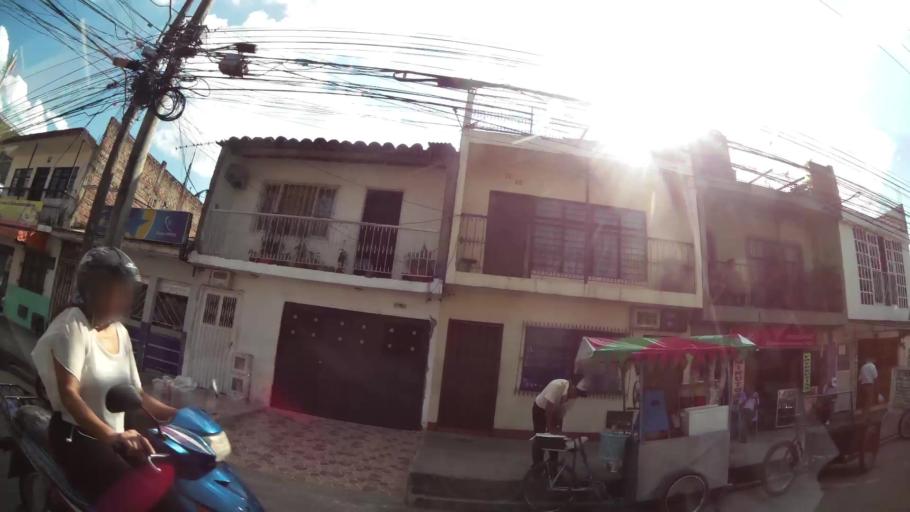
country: CO
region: Valle del Cauca
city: Cali
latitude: 3.4208
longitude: -76.4966
